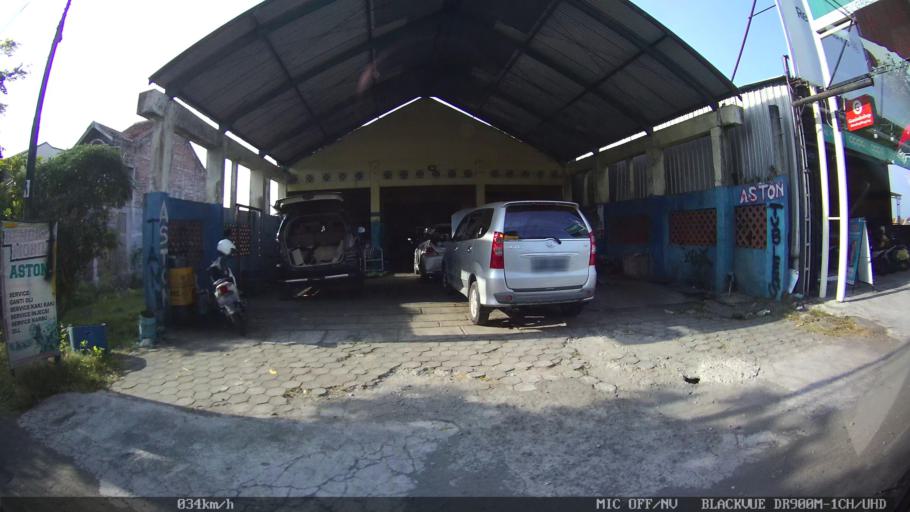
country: ID
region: Daerah Istimewa Yogyakarta
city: Bantul
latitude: -7.8780
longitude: 110.3275
